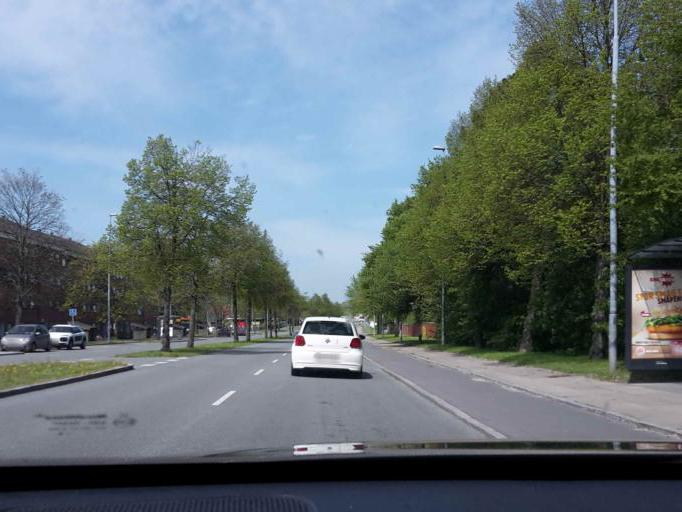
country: DK
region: South Denmark
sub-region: Odense Kommune
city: Odense
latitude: 55.3775
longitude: 10.4088
